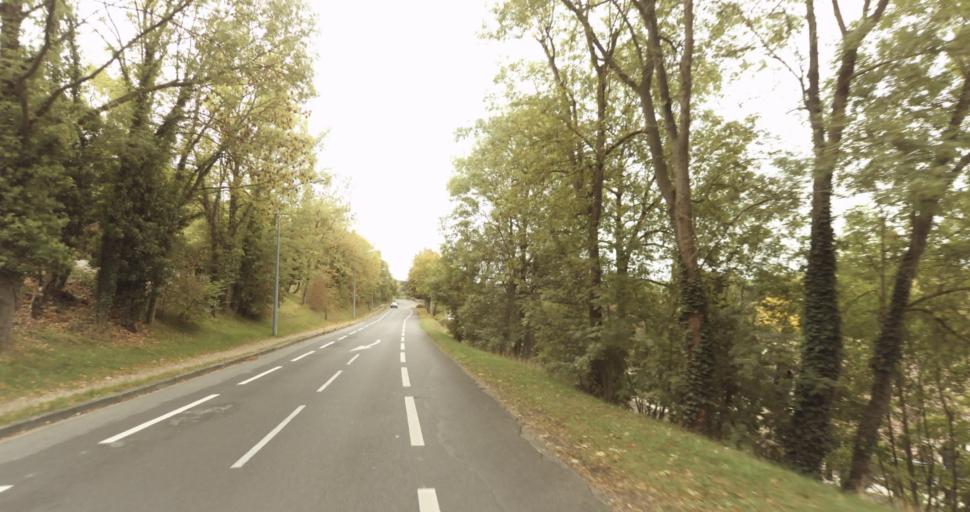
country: FR
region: Centre
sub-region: Departement d'Eure-et-Loir
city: Vernouillet
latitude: 48.7197
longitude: 1.3574
